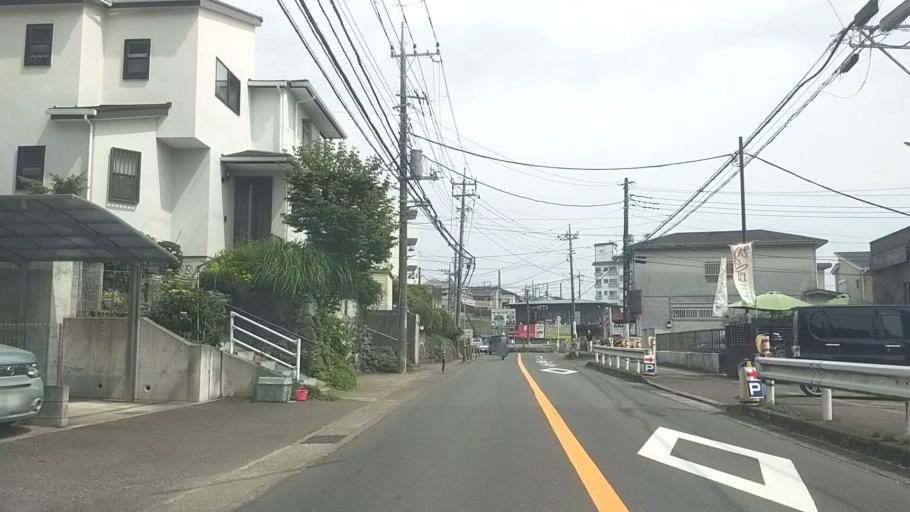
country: JP
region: Kanagawa
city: Fujisawa
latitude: 35.3871
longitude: 139.4686
